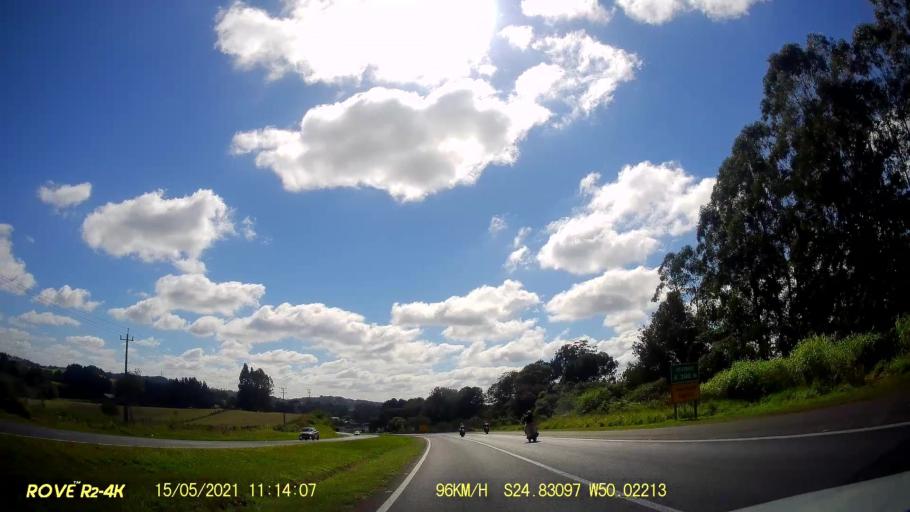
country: BR
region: Parana
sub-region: Castro
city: Castro
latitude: -24.8311
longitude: -50.0220
